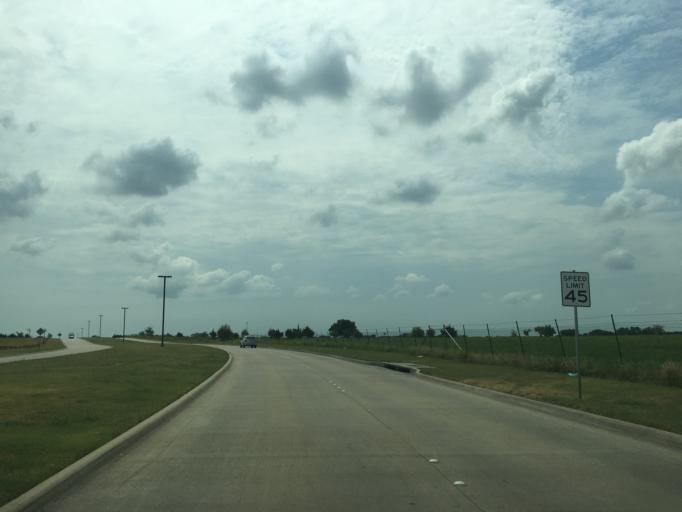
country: US
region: Texas
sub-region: Rockwall County
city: Rockwall
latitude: 32.9578
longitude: -96.4515
